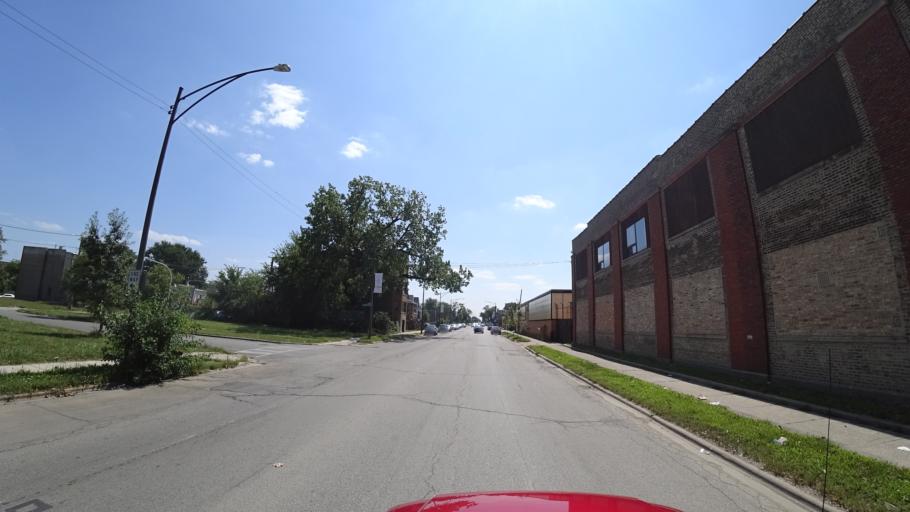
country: US
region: Illinois
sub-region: Cook County
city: Cicero
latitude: 41.8644
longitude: -87.7349
